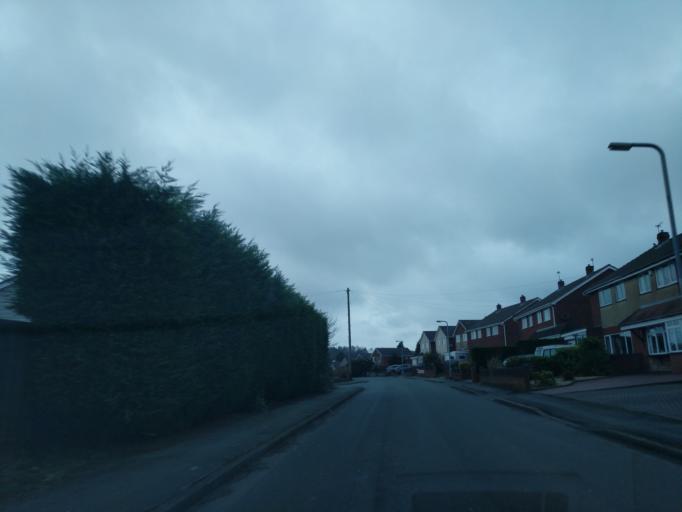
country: GB
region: England
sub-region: Staffordshire
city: Cannock
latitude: 52.7161
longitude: -2.0178
